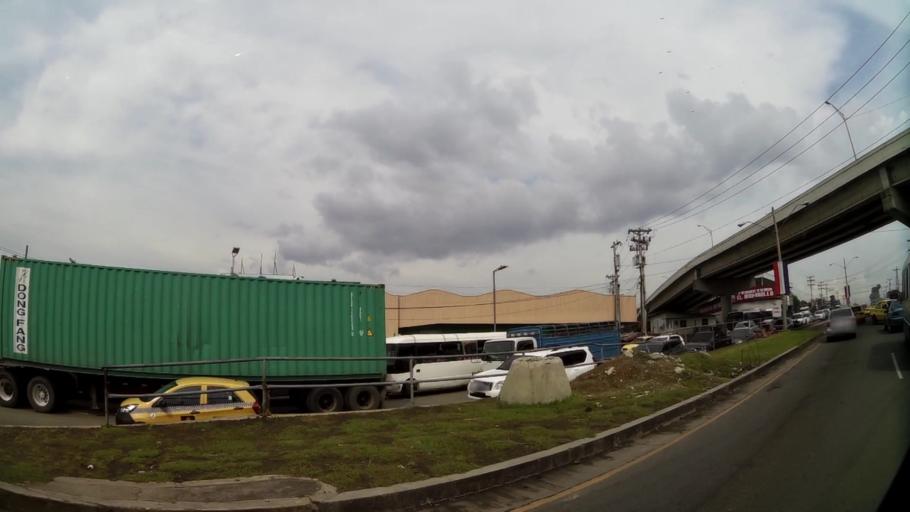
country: PA
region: Panama
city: Tocumen
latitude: 9.1031
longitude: -79.3661
